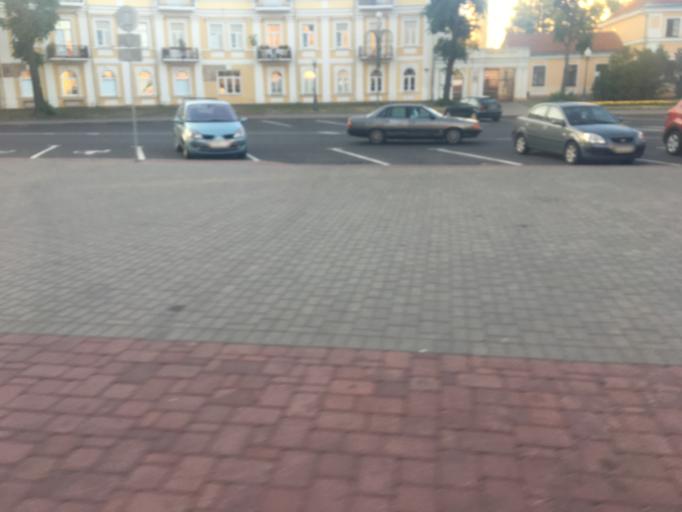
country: BY
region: Grodnenskaya
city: Hrodna
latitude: 53.6845
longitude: 23.8342
